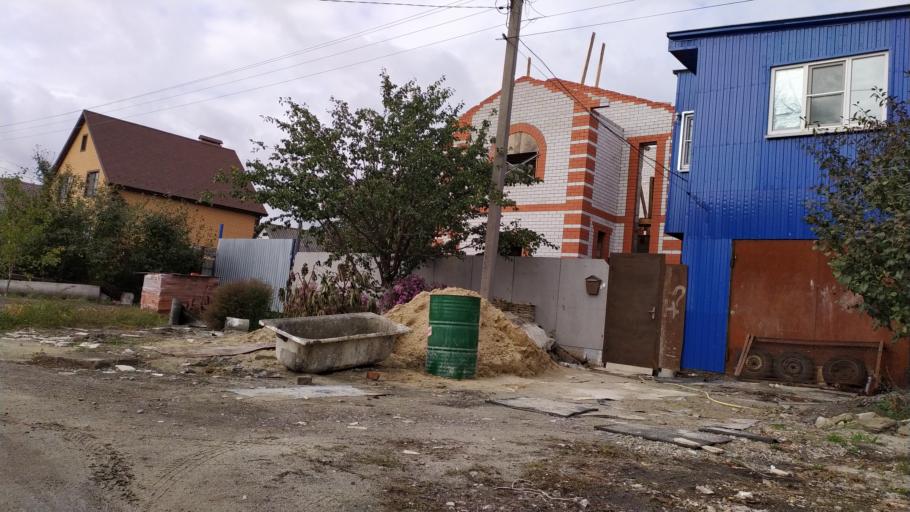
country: RU
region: Kursk
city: Kursk
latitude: 51.6421
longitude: 36.1555
